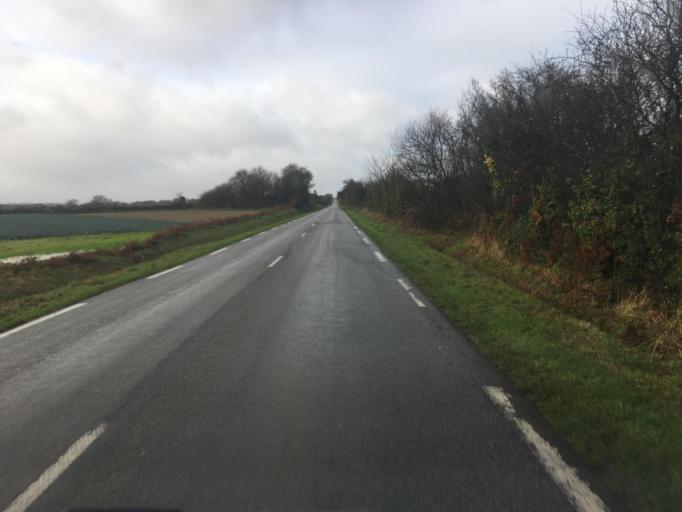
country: FR
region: Lower Normandy
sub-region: Departement de la Manche
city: Saint-Pierre-Eglise
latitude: 49.6697
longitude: -1.3575
